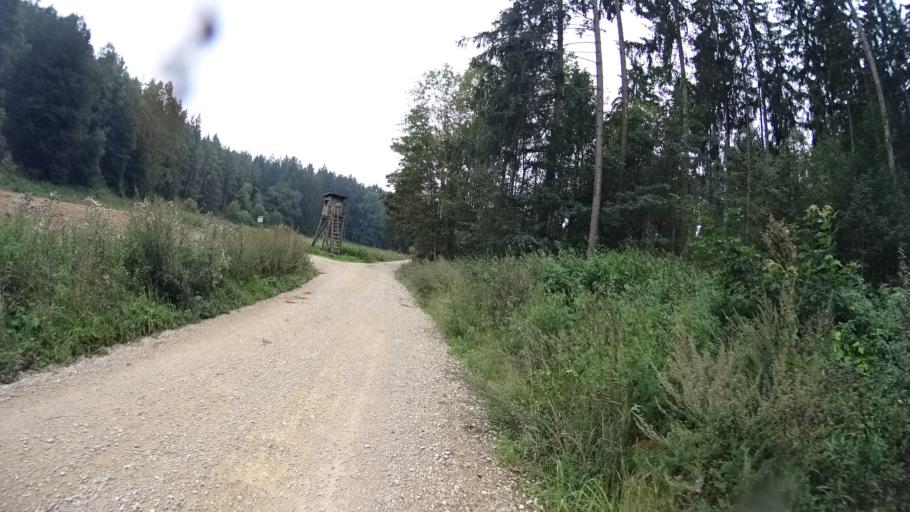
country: DE
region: Bavaria
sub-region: Upper Bavaria
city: Bohmfeld
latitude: 48.8871
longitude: 11.3504
